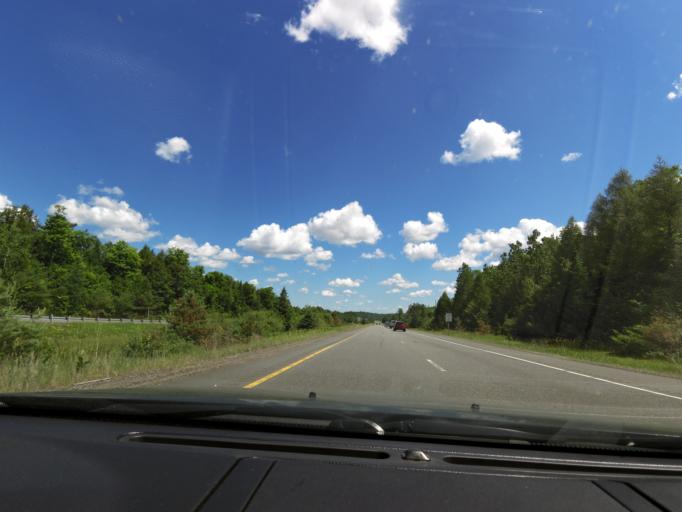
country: CA
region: Ontario
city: Huntsville
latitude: 45.2255
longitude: -79.3105
